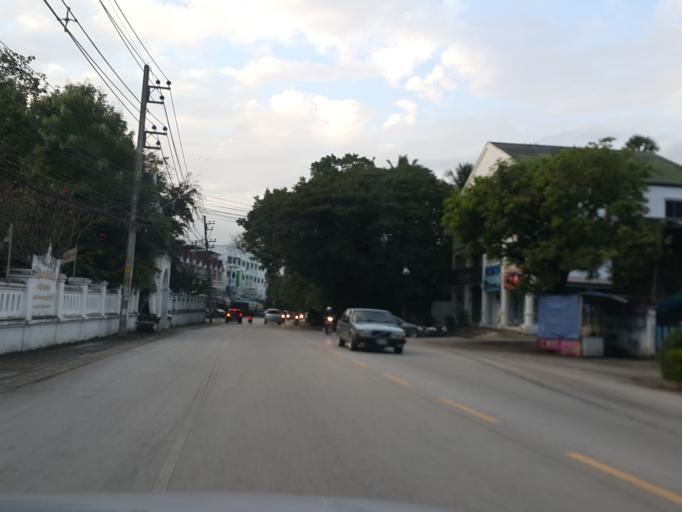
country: TH
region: Lampang
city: Lampang
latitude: 18.2834
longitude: 99.5056
